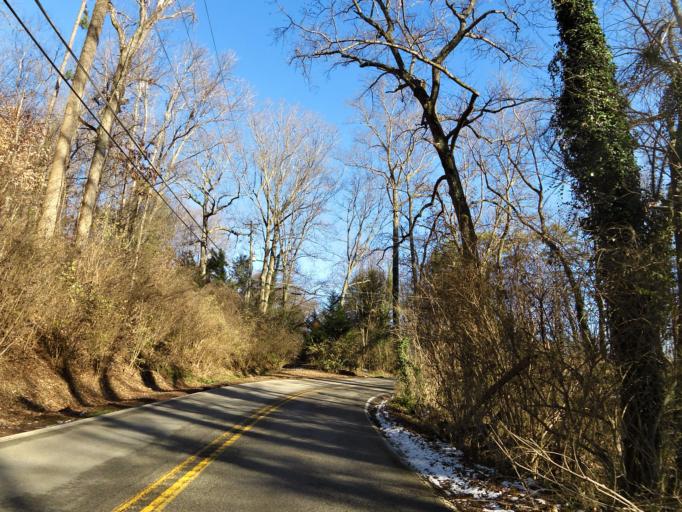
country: US
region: Tennessee
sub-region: Knox County
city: Knoxville
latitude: 35.9103
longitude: -83.9964
